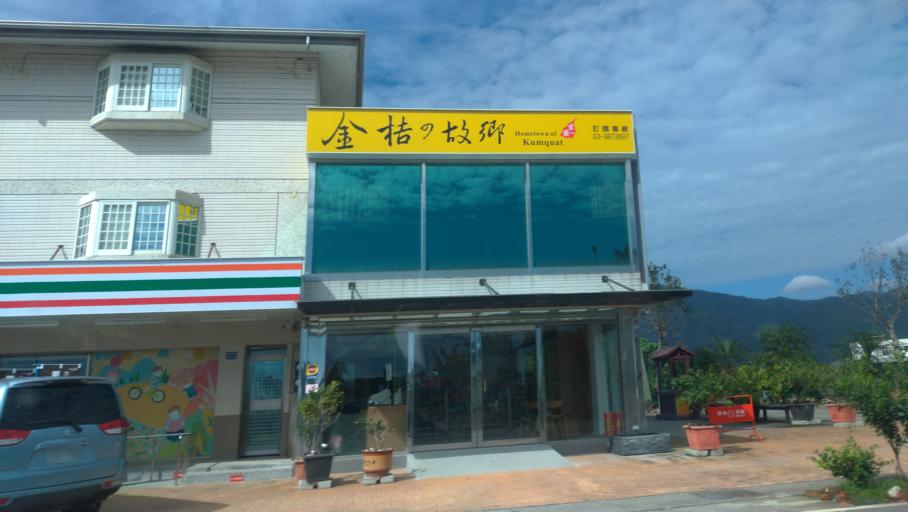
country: TW
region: Taiwan
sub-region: Yilan
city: Yilan
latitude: 24.8171
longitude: 121.7956
